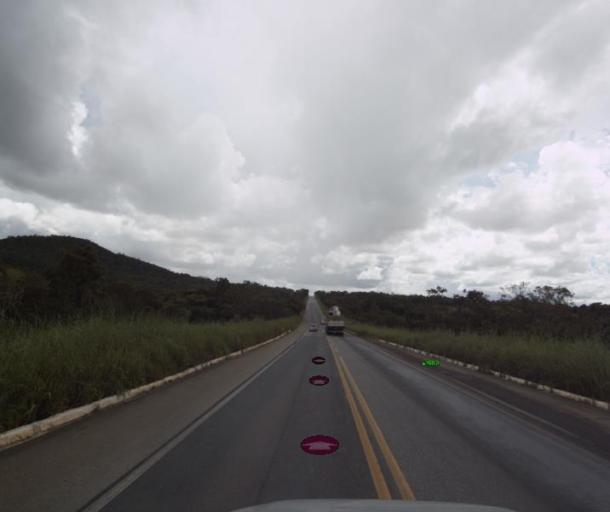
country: BR
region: Goias
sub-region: Uruacu
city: Uruacu
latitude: -14.2290
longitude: -49.1335
